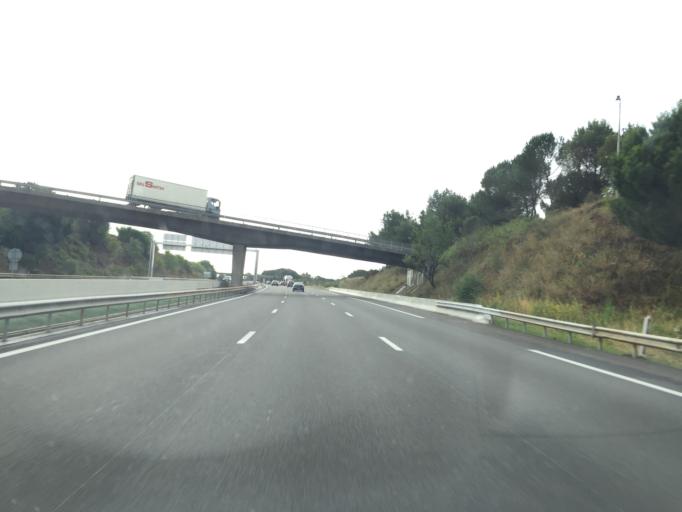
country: FR
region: Provence-Alpes-Cote d'Azur
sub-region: Departement du Var
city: Puget-sur-Argens
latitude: 43.4591
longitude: 6.6884
